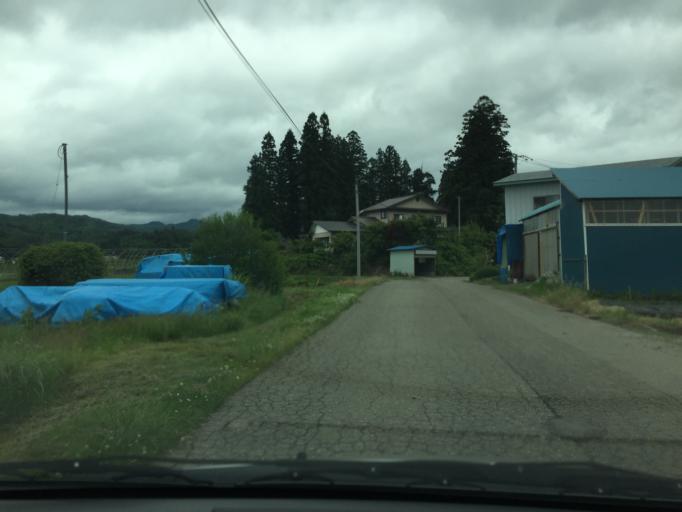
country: JP
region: Fukushima
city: Kitakata
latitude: 37.4431
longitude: 139.8178
